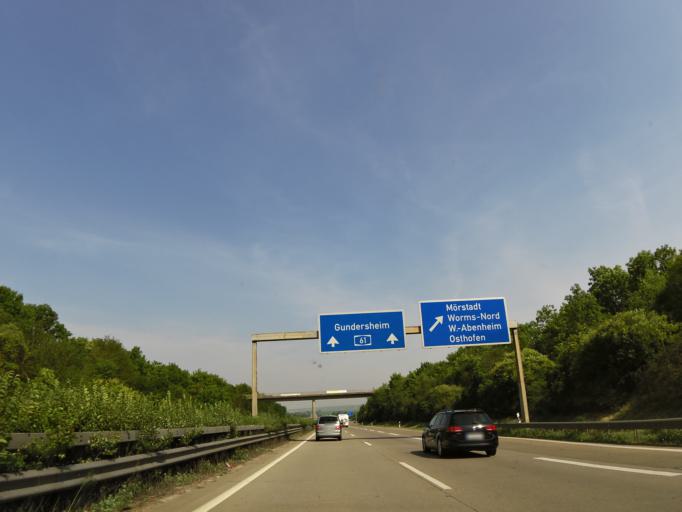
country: DE
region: Rheinland-Pfalz
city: Morstadt
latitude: 49.6612
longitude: 8.2793
